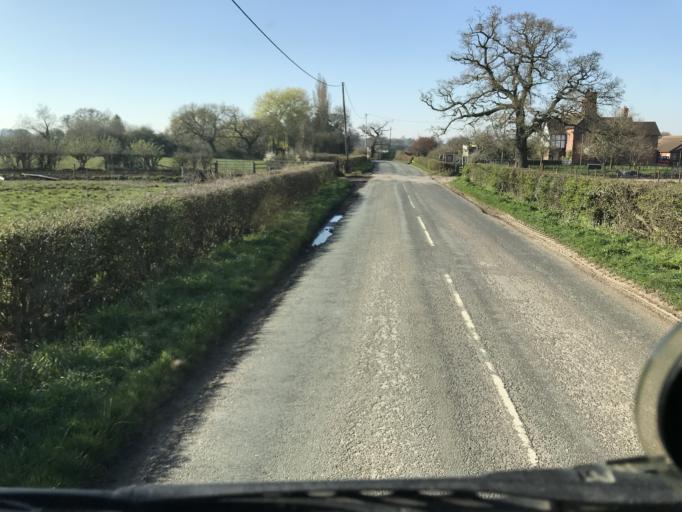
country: GB
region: England
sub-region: Cheshire West and Chester
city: Waverton
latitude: 53.1622
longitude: -2.8267
